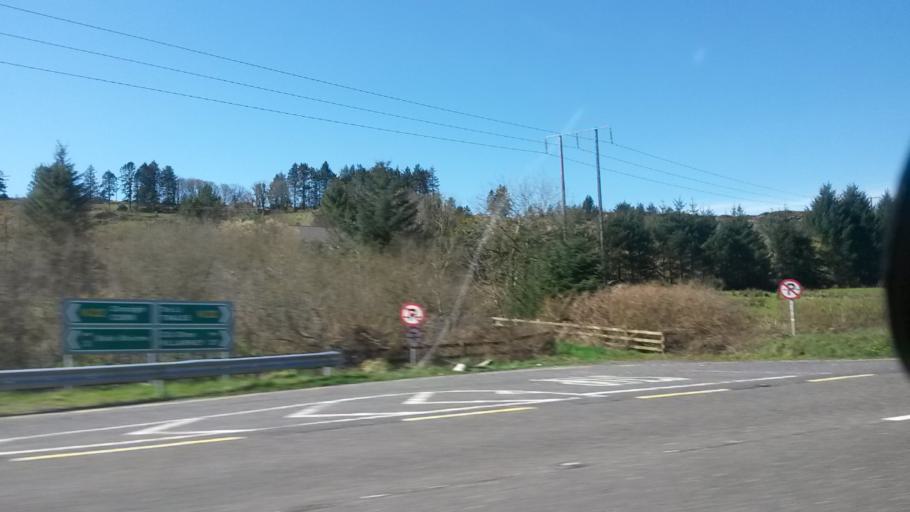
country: IE
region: Munster
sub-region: County Cork
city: Millstreet
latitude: 51.9593
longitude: -9.1971
